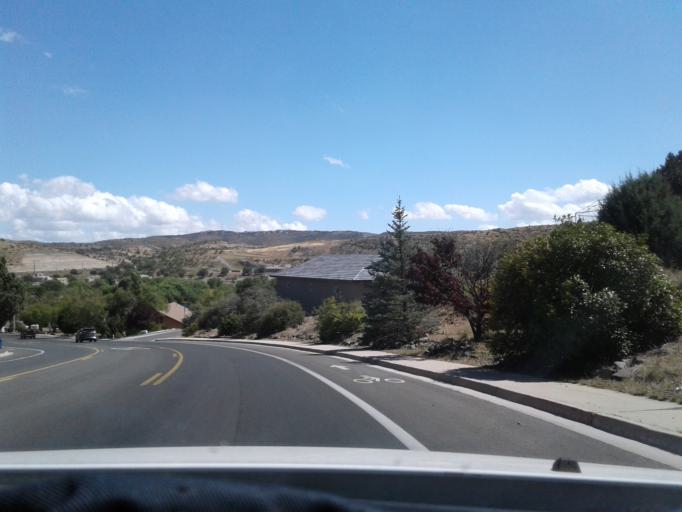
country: US
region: Arizona
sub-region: Yavapai County
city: Prescott
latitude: 34.5729
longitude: -112.4397
